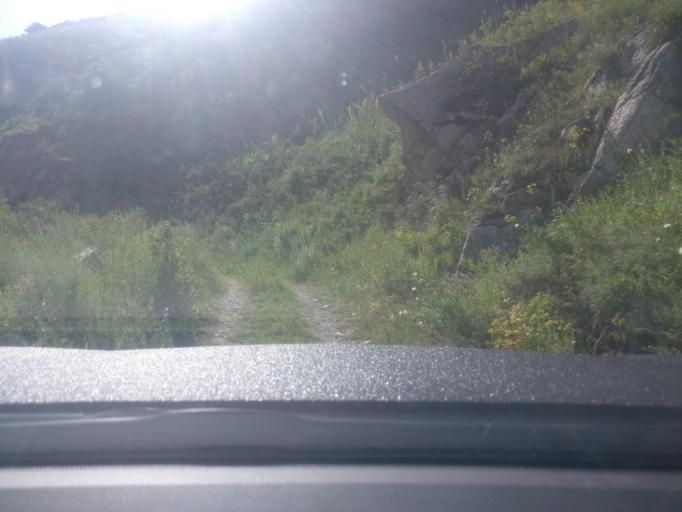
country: KZ
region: Almaty Qalasy
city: Almaty
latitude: 43.1072
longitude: 76.9371
